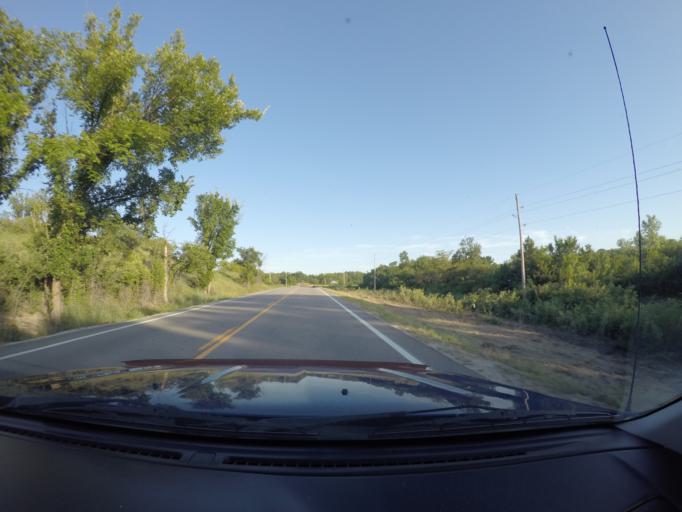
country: US
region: Kansas
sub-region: Pottawatomie County
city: Wamego
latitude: 39.1181
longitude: -96.2904
